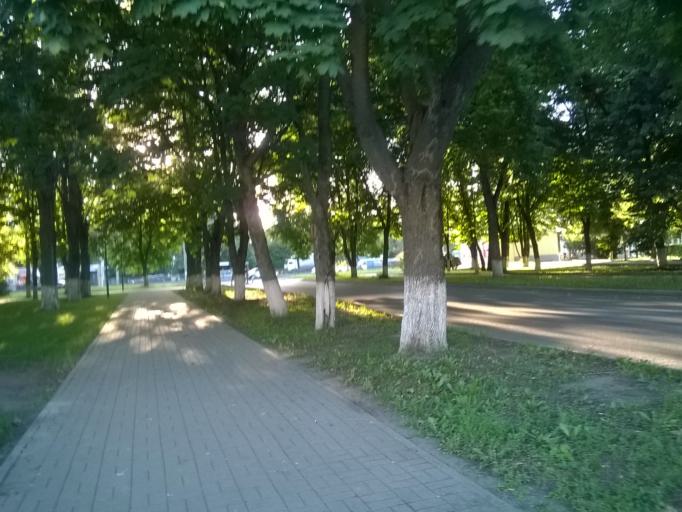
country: RU
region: Kursk
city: Kursk
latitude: 51.6709
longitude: 36.1440
